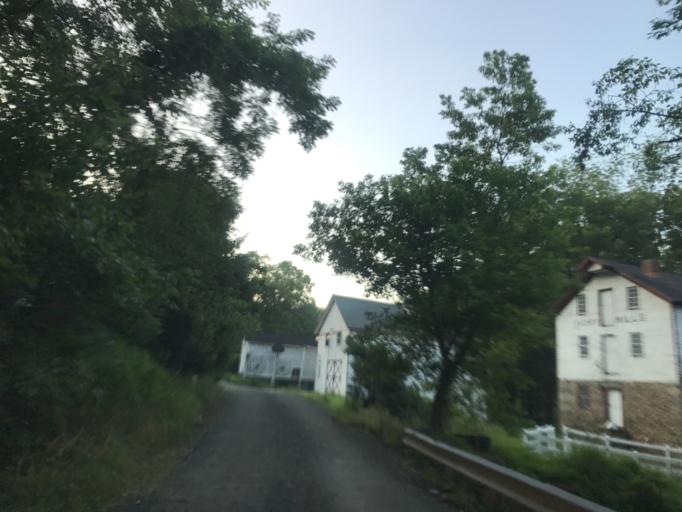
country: US
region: Maryland
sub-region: Harford County
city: Jarrettsville
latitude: 39.6735
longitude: -76.5359
